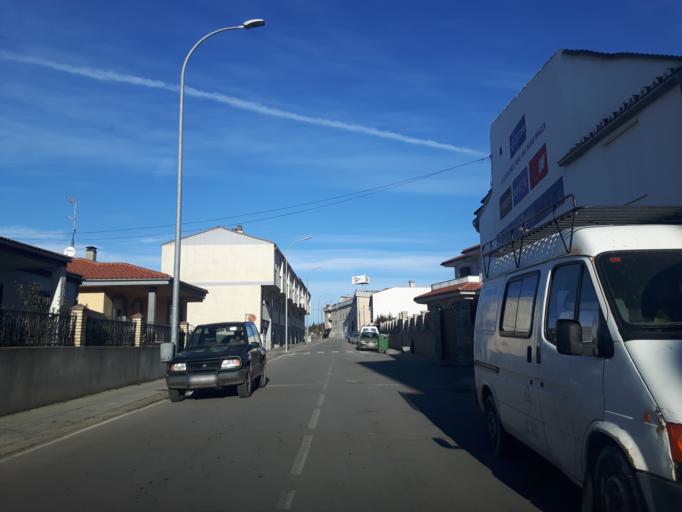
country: ES
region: Castille and Leon
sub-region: Provincia de Salamanca
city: Vitigudino
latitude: 41.0072
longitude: -6.4368
